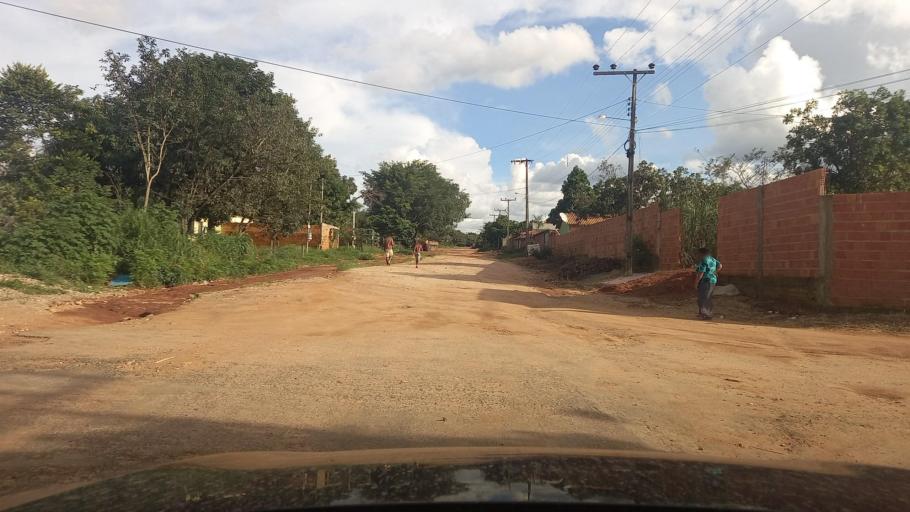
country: BR
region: Goias
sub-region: Cavalcante
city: Cavalcante
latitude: -13.7957
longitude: -47.4426
